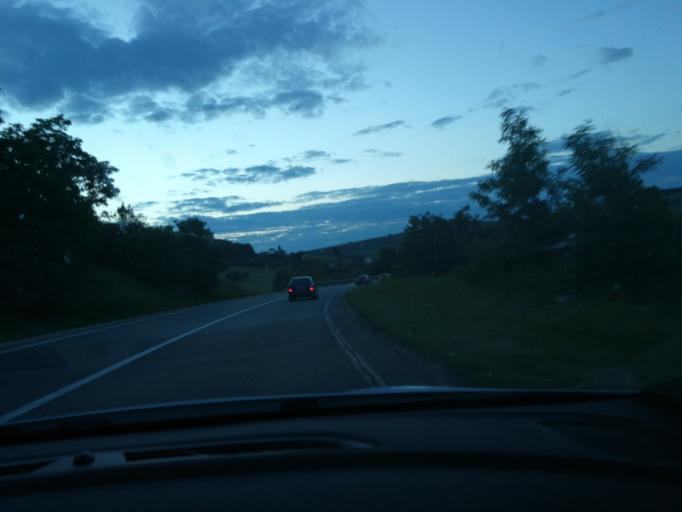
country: RO
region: Brasov
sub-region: Oras Rupea
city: Rupea
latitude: 46.0322
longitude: 25.2043
